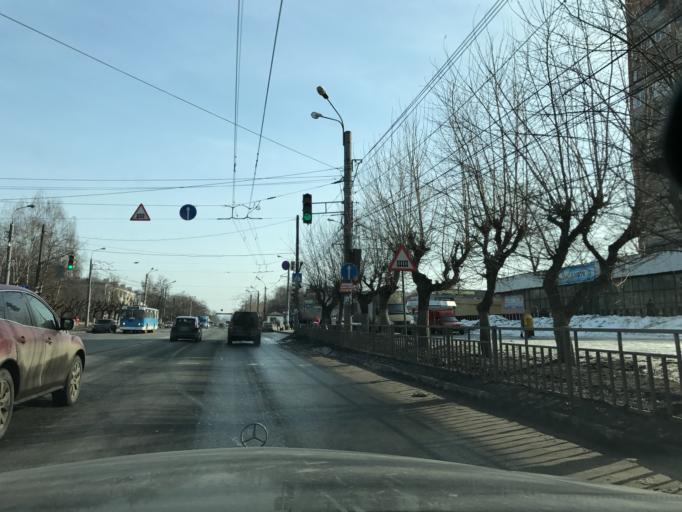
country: RU
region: Nizjnij Novgorod
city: Nizhniy Novgorod
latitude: 56.3141
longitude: 43.8821
